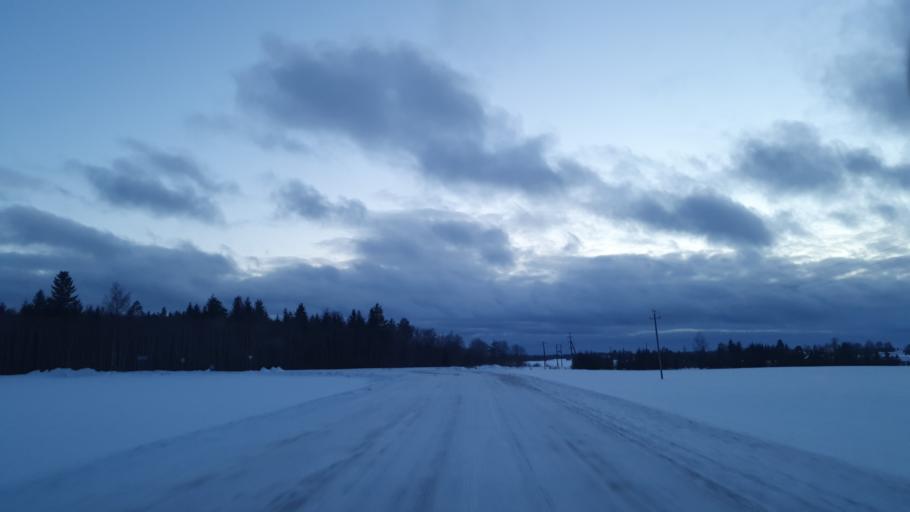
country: EE
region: Jogevamaa
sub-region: Jogeva linn
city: Jogeva
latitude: 58.6148
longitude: 26.4081
